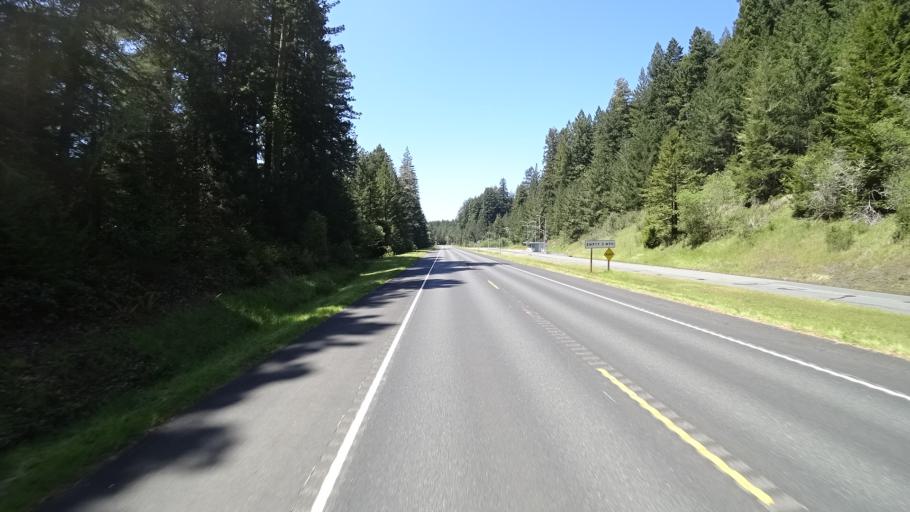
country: US
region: California
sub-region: Humboldt County
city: Blue Lake
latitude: 40.8843
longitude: -123.9619
